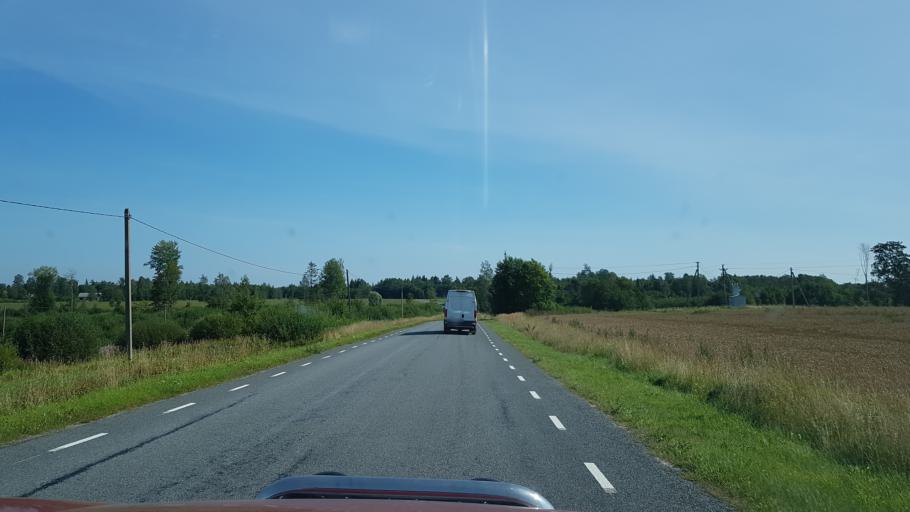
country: EE
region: Viljandimaa
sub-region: Suure-Jaani vald
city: Suure-Jaani
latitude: 58.4962
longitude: 25.5708
